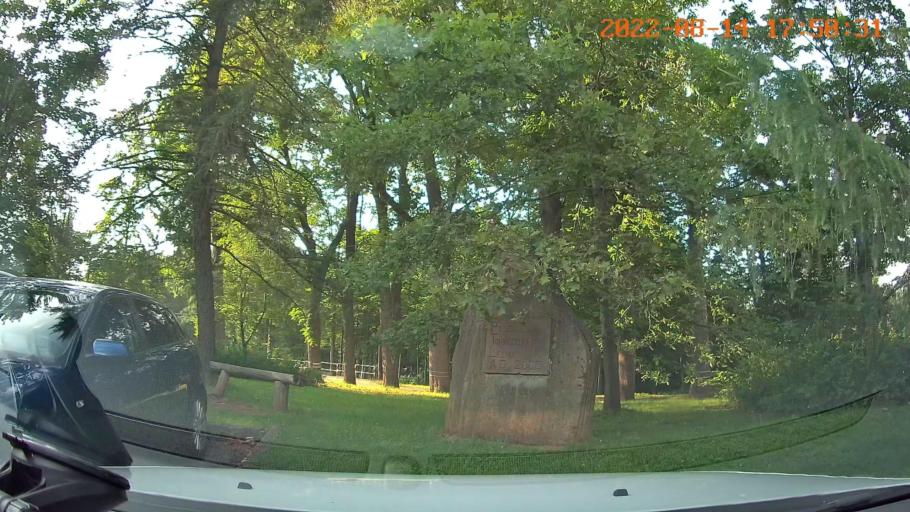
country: PL
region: Swietokrzyskie
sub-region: Powiat kielecki
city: Kaniow
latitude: 50.9870
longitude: 20.6510
